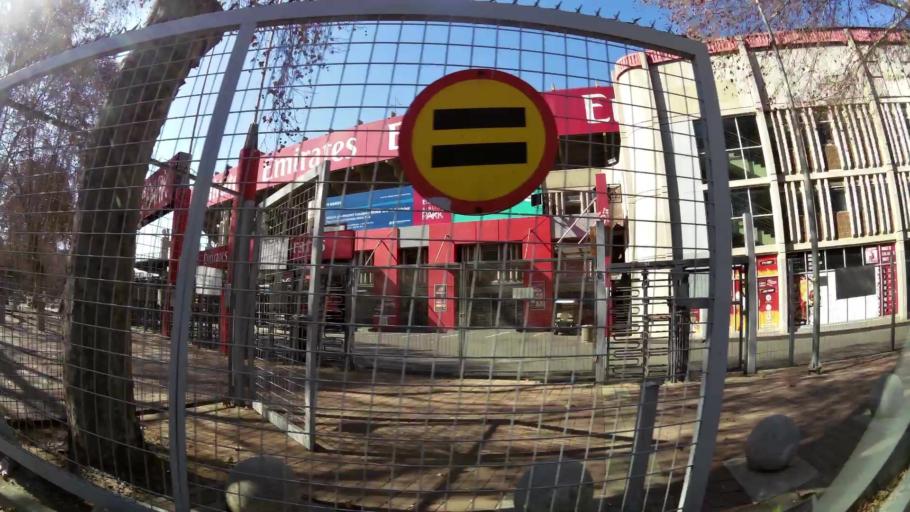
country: ZA
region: Gauteng
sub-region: City of Johannesburg Metropolitan Municipality
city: Johannesburg
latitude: -26.1974
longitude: 28.0593
